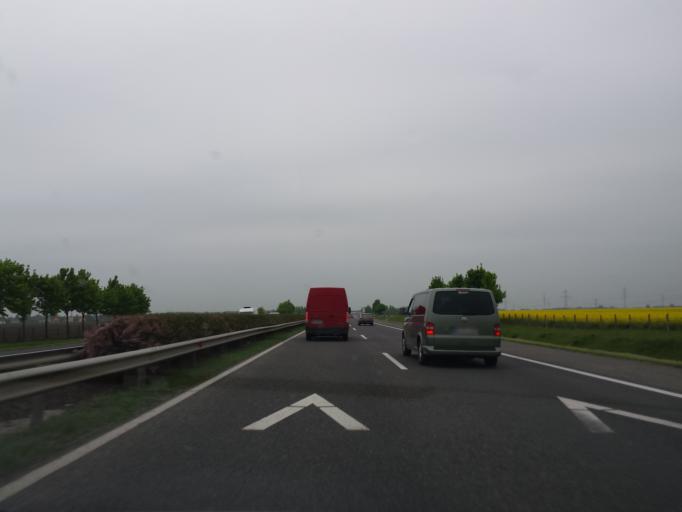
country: HU
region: Gyor-Moson-Sopron
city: Mosonszentmiklos
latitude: 47.7297
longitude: 17.4483
